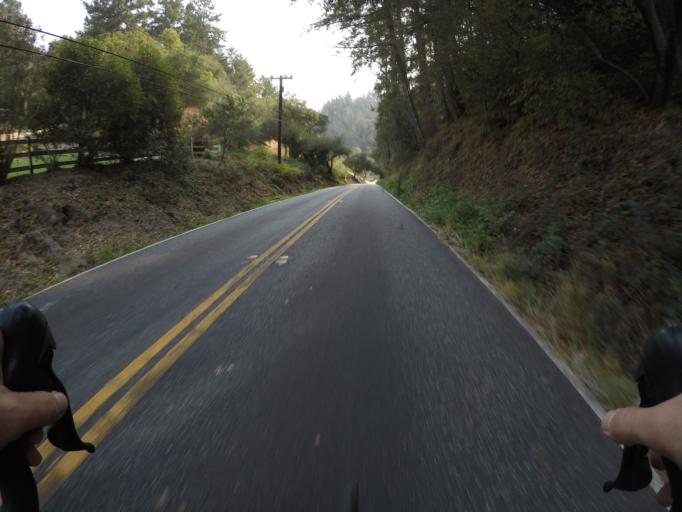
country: US
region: California
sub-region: Santa Cruz County
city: Pasatiempo
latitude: 37.0203
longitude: -122.0195
